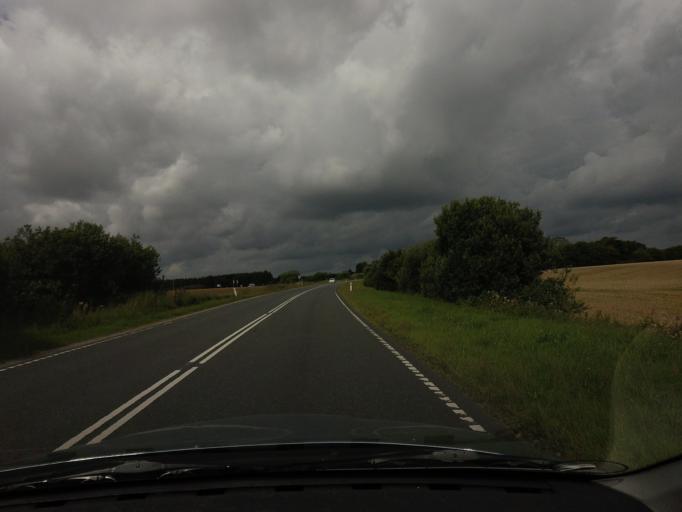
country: DK
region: North Denmark
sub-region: Hjorring Kommune
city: Hjorring
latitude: 57.4229
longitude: 10.0463
